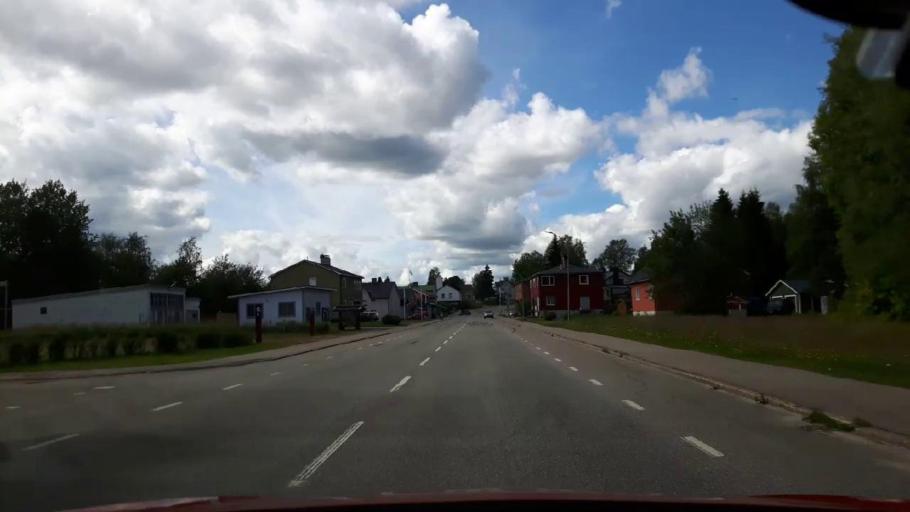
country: SE
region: Jaemtland
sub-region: Harjedalens Kommun
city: Sveg
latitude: 61.8519
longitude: 14.0782
